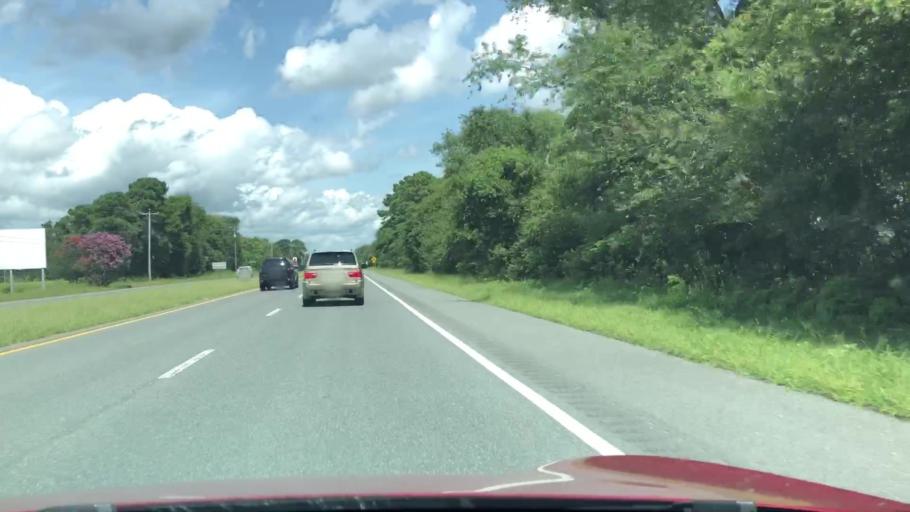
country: US
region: Virginia
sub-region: Northampton County
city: Cape Charles
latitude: 37.1838
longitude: -75.9684
